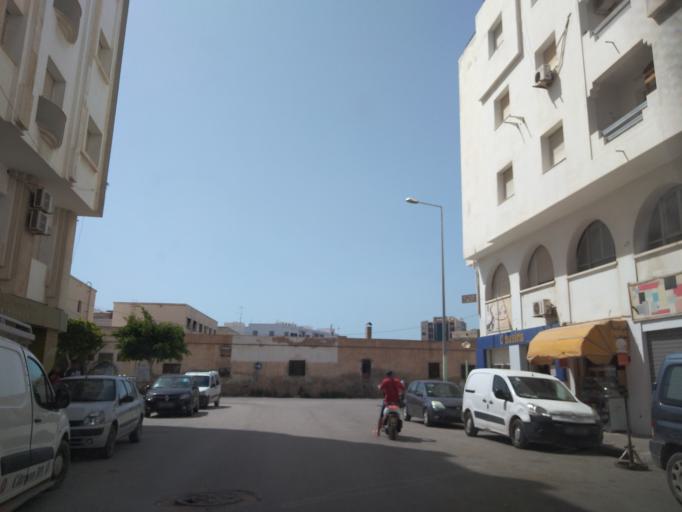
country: TN
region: Safaqis
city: Sfax
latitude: 34.7353
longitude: 10.7556
